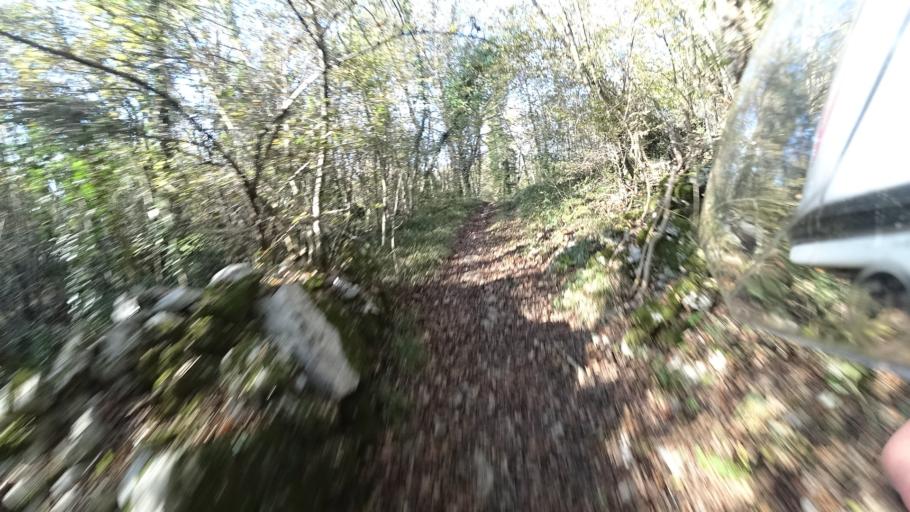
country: HR
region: Primorsko-Goranska
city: Matulji
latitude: 45.3954
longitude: 14.2974
